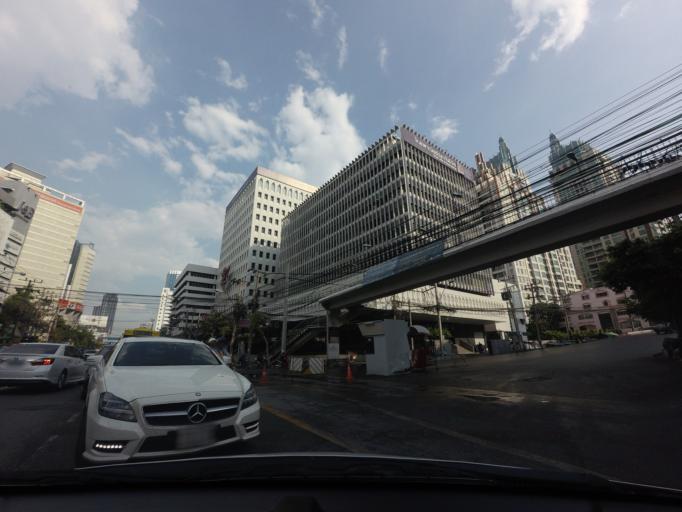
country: TH
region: Bangkok
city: Ratchathewi
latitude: 13.7494
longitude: 100.5447
